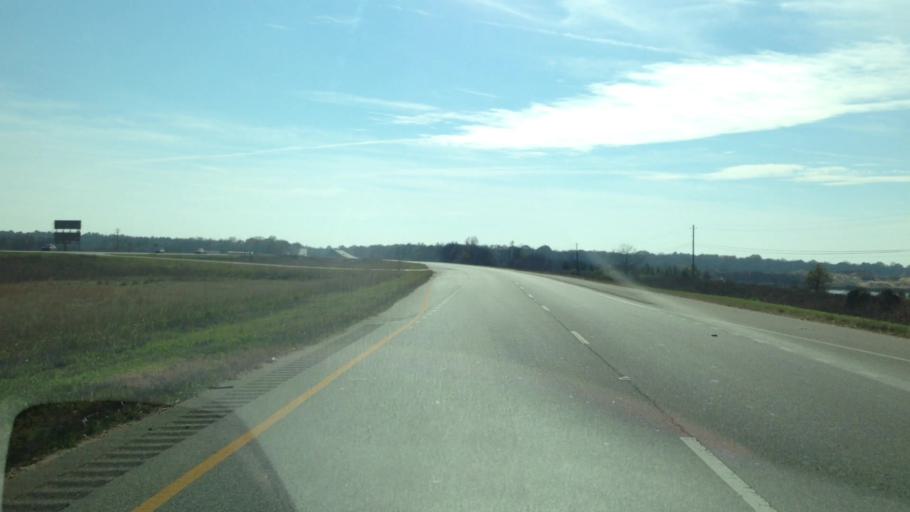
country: US
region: Alabama
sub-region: Autauga County
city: Prattville
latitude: 32.4237
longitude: -86.4120
